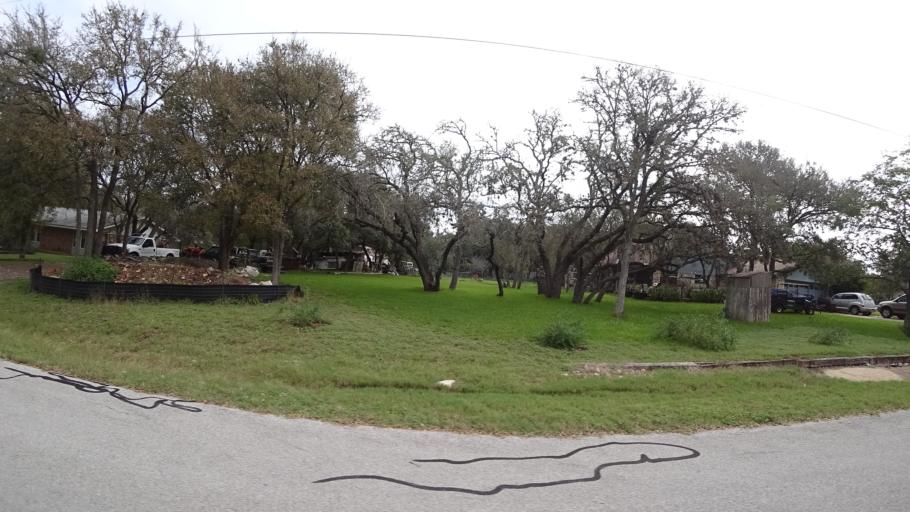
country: US
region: Texas
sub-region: Travis County
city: Shady Hollow
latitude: 30.1367
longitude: -97.8872
